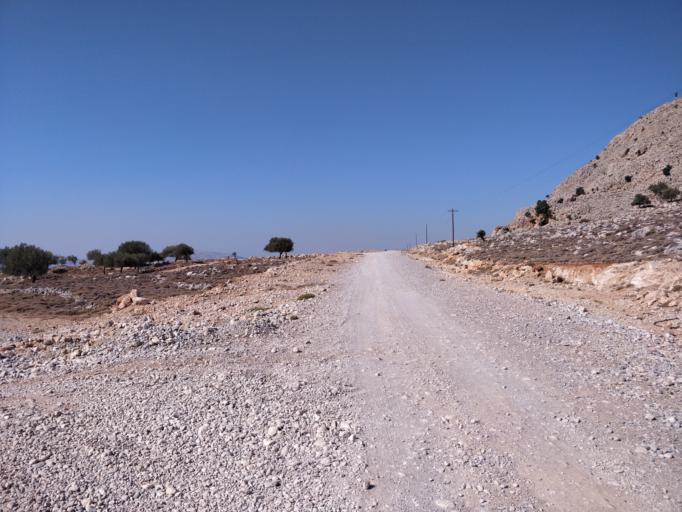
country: GR
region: South Aegean
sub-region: Nomos Dodekanisou
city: Archangelos
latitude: 36.1933
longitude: 28.1250
